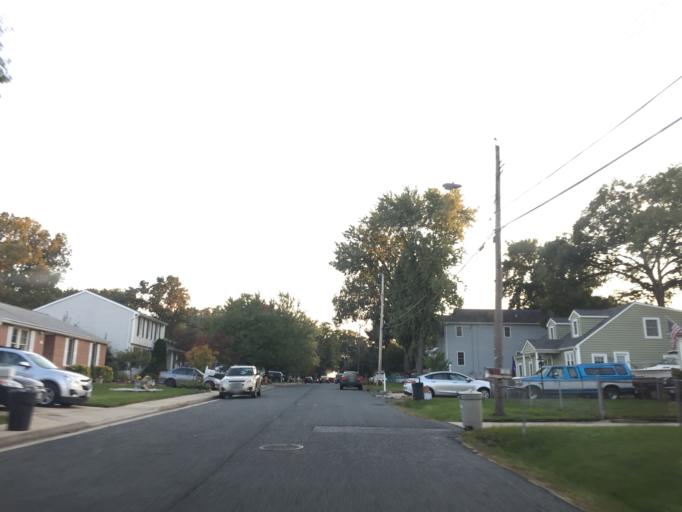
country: US
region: Maryland
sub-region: Baltimore County
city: Essex
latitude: 39.3196
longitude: -76.4713
